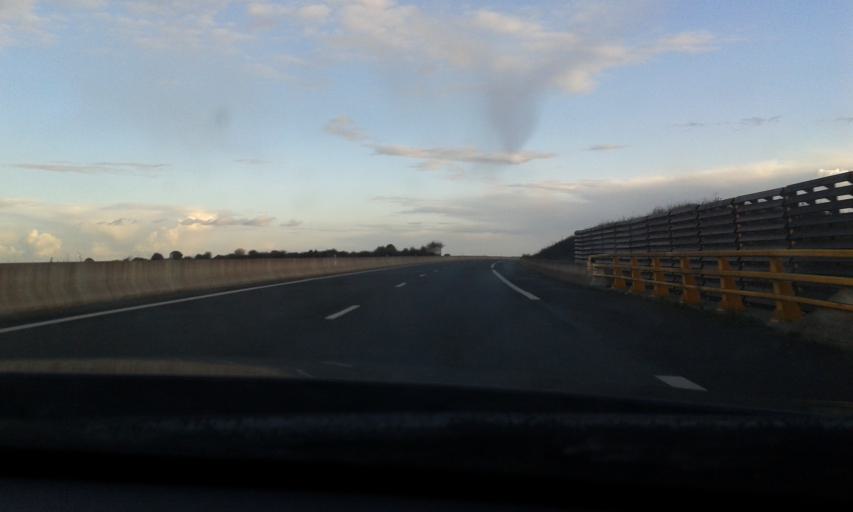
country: FR
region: Centre
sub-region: Departement d'Eure-et-Loir
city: Voves
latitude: 48.2689
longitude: 1.7551
